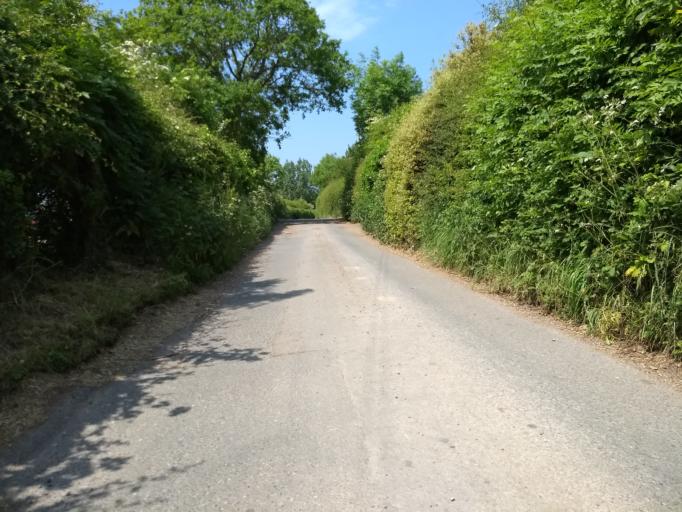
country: GB
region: England
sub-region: Isle of Wight
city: East Cowes
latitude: 50.7366
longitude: -1.2704
